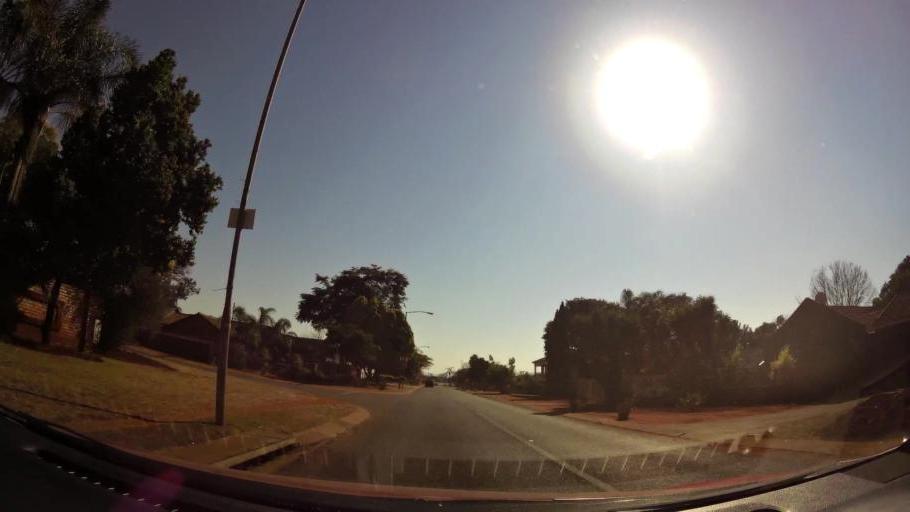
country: ZA
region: North-West
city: Ga-Rankuwa
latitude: -25.6473
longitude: 28.1094
